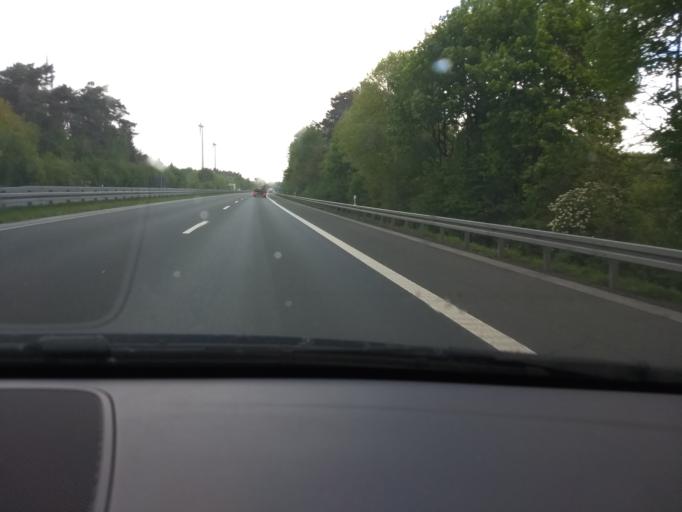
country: DE
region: North Rhine-Westphalia
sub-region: Regierungsbezirk Munster
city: Heiden
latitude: 51.7761
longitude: 6.9664
